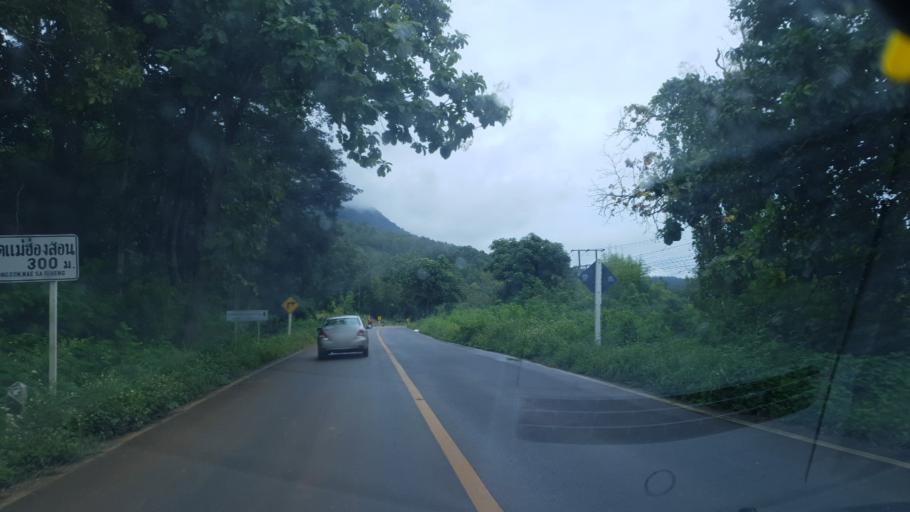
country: TH
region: Mae Hong Son
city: Pa Pae
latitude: 18.1983
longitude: 97.9379
